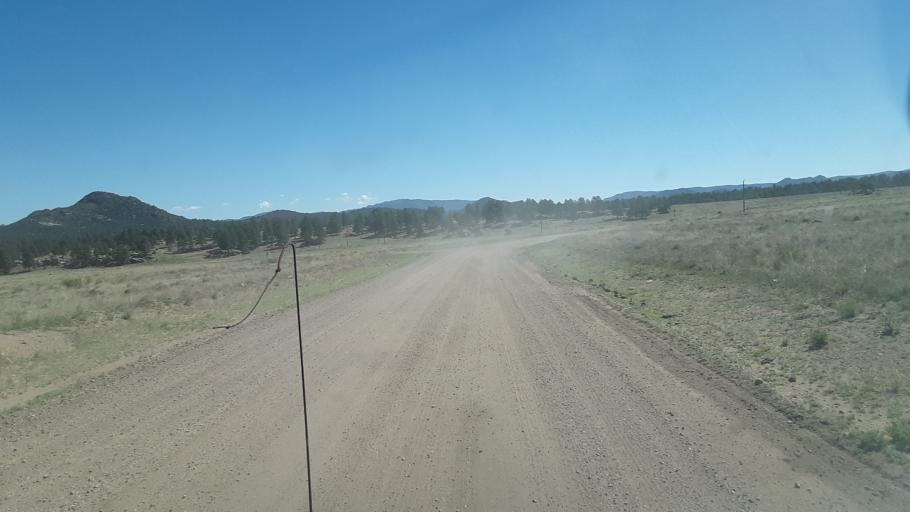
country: US
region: Colorado
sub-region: Custer County
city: Westcliffe
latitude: 38.2013
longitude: -105.4498
